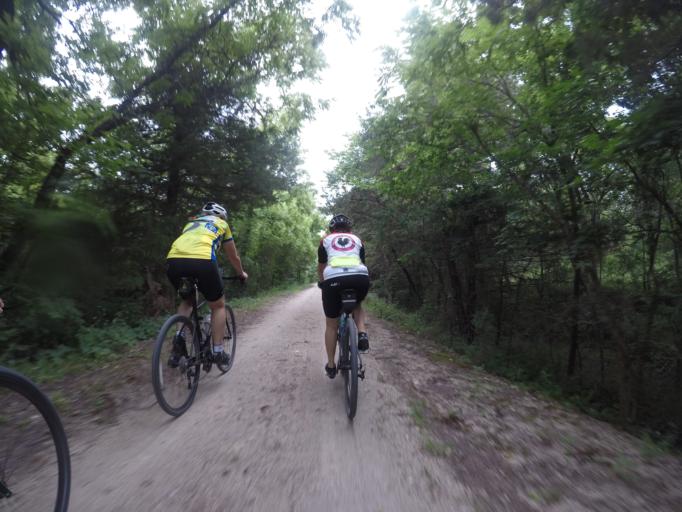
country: US
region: Kansas
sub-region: Anderson County
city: Garnett
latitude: 38.2449
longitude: -95.2553
